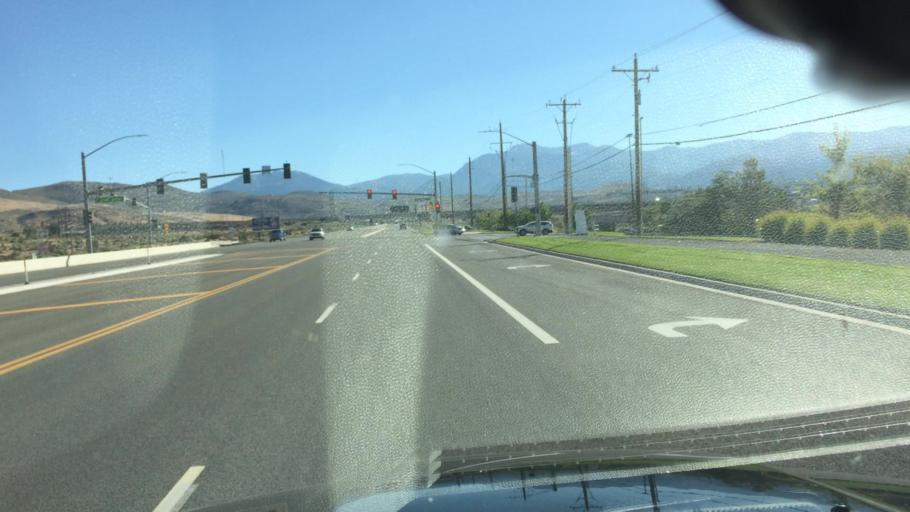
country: US
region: Nevada
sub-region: Washoe County
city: Sparks
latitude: 39.4008
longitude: -119.7506
